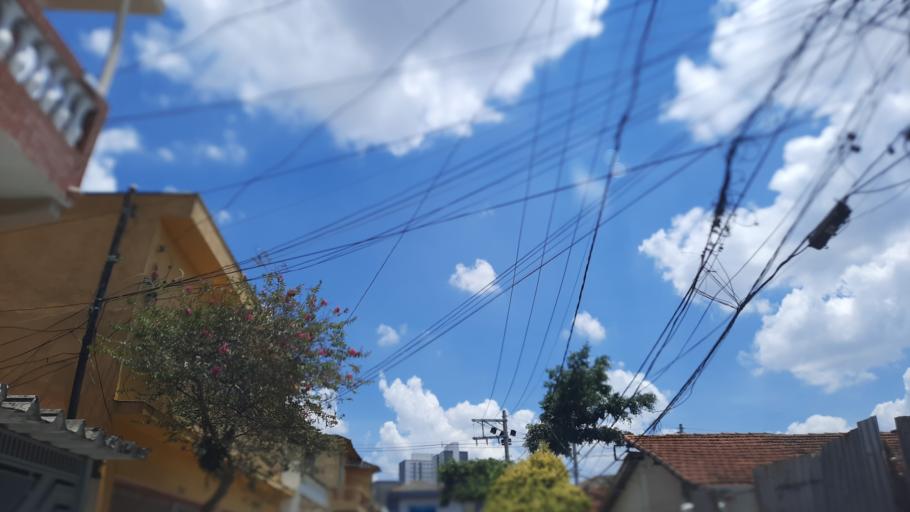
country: BR
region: Sao Paulo
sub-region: Sao Paulo
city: Sao Paulo
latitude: -23.4916
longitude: -46.6837
